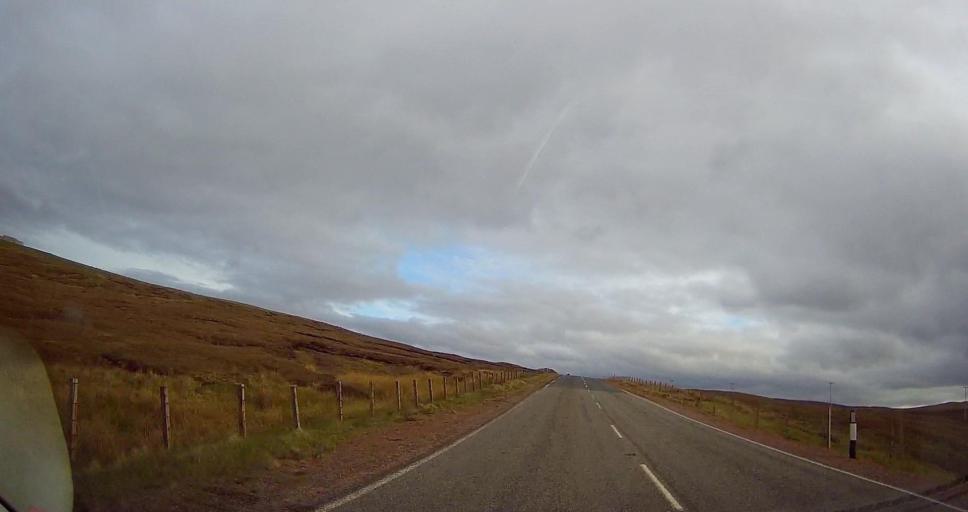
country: GB
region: Scotland
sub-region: Shetland Islands
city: Lerwick
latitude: 60.4546
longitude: -1.2126
